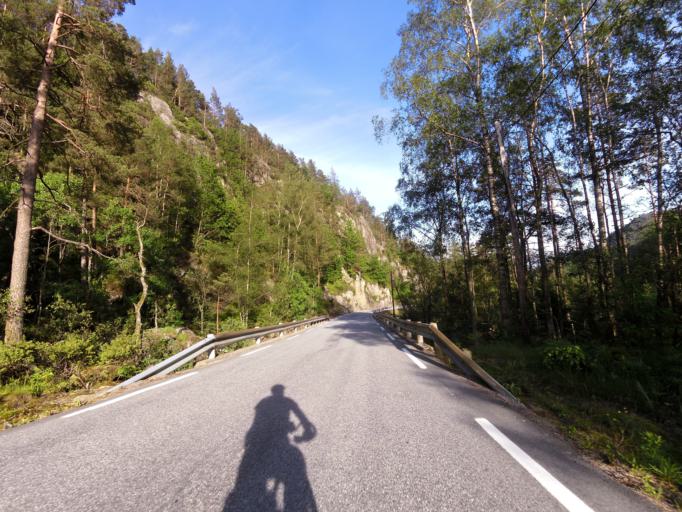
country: NO
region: Vest-Agder
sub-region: Flekkefjord
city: Flekkefjord
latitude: 58.2796
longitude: 6.6264
